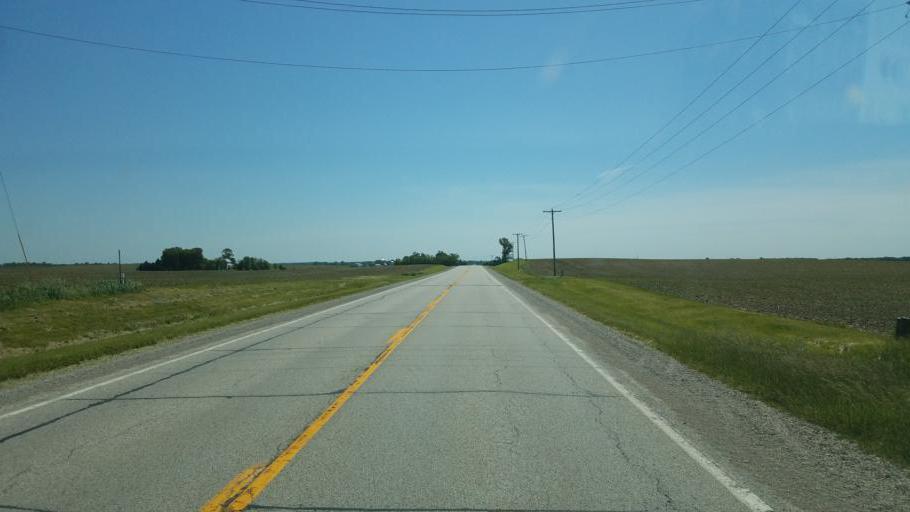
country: US
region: Illinois
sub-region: McLean County
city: Heyworth
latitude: 40.3119
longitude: -89.0748
